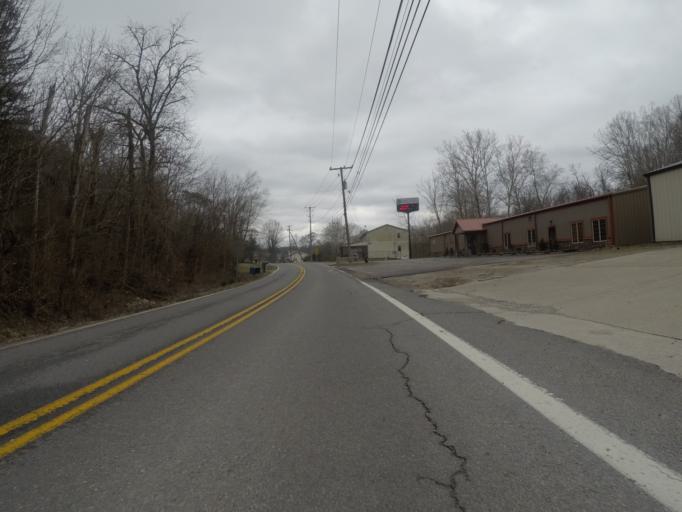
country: US
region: West Virginia
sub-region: Cabell County
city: Barboursville
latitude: 38.4251
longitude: -82.2918
